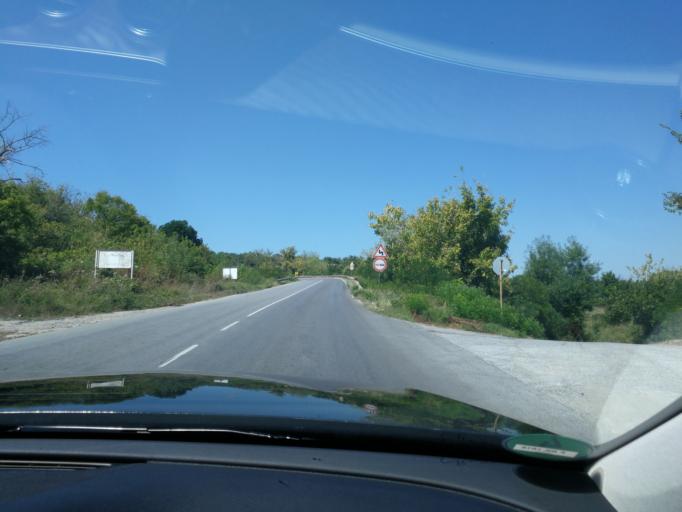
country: BG
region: Khaskovo
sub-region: Obshtina Topolovgrad
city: Topolovgrad
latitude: 42.0827
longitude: 26.3265
